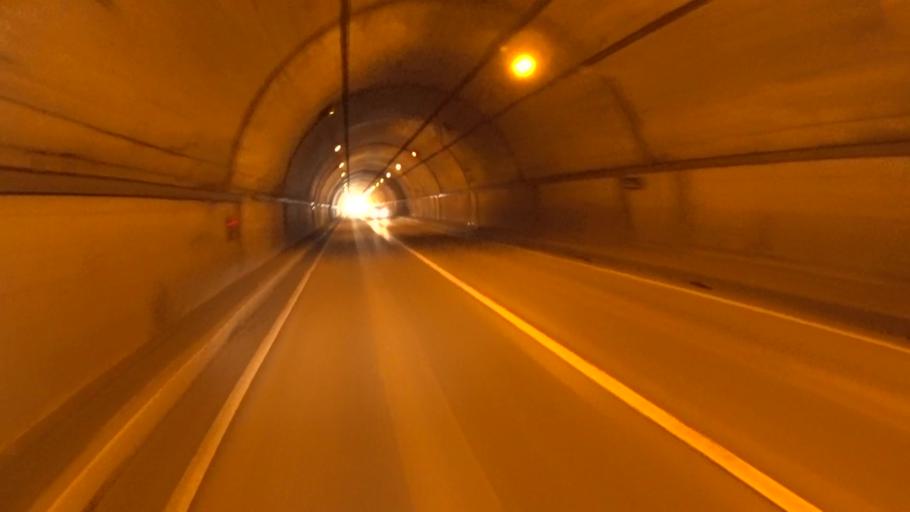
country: JP
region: Kyoto
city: Fukuchiyama
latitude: 35.4108
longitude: 135.0852
